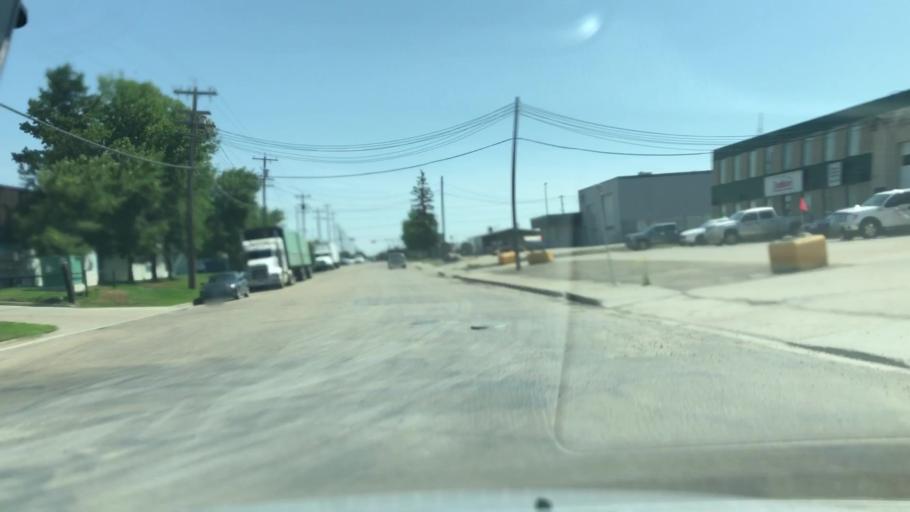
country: CA
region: Alberta
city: St. Albert
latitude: 53.5737
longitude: -113.5945
